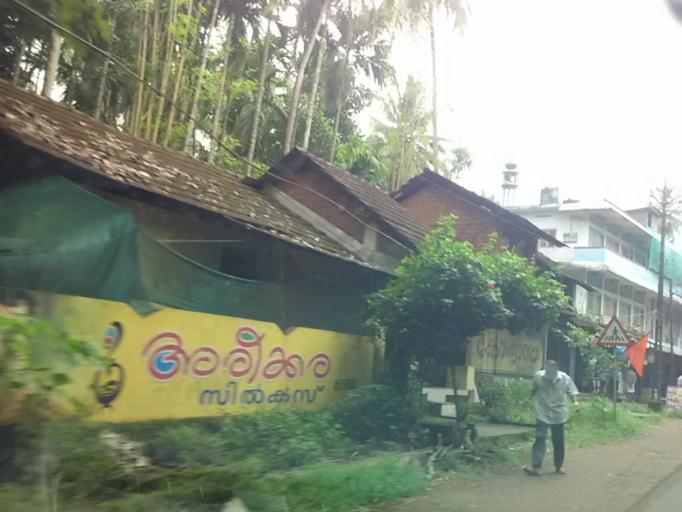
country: IN
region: Kerala
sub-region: Kozhikode
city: Mavoor
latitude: 11.3152
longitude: 75.9265
